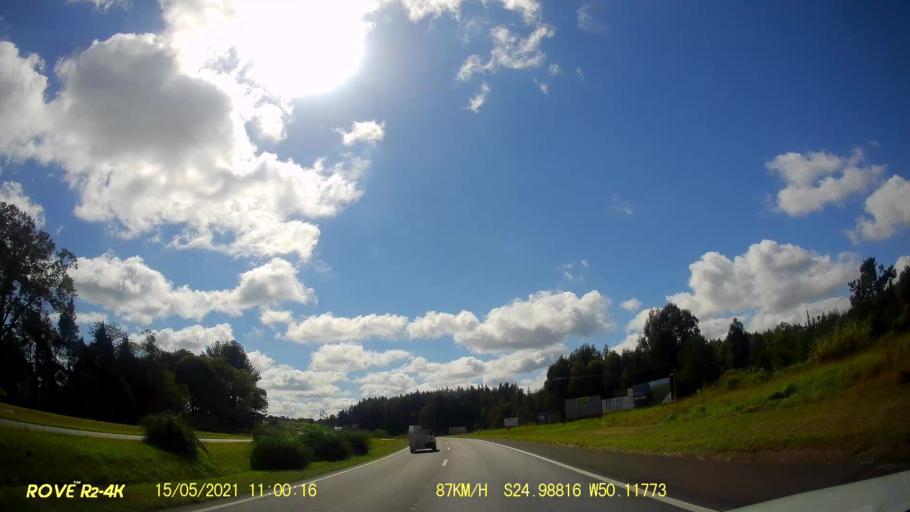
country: BR
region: Parana
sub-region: Carambei
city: Carambei
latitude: -24.9881
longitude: -50.1178
